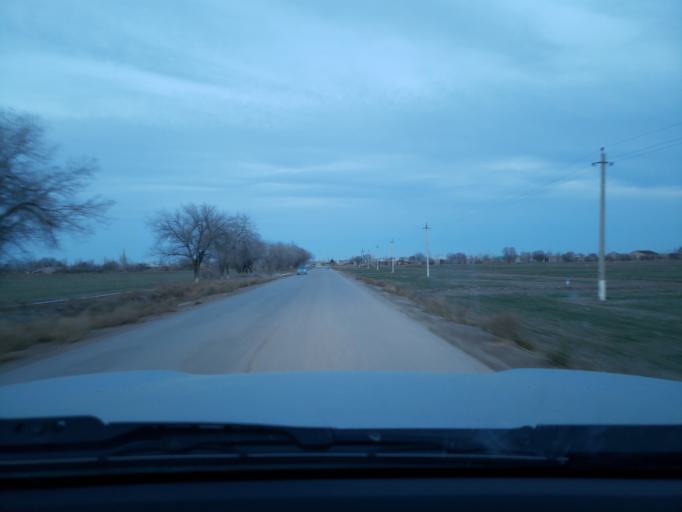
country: TM
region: Dasoguz
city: Tagta
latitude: 41.6275
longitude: 60.0646
